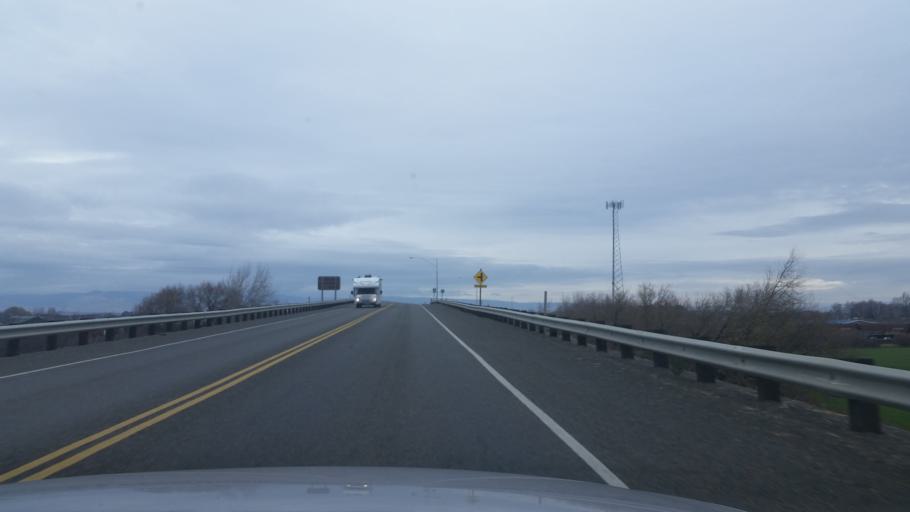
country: US
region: Washington
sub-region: Kittitas County
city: Ellensburg
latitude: 47.0096
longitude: -120.5789
